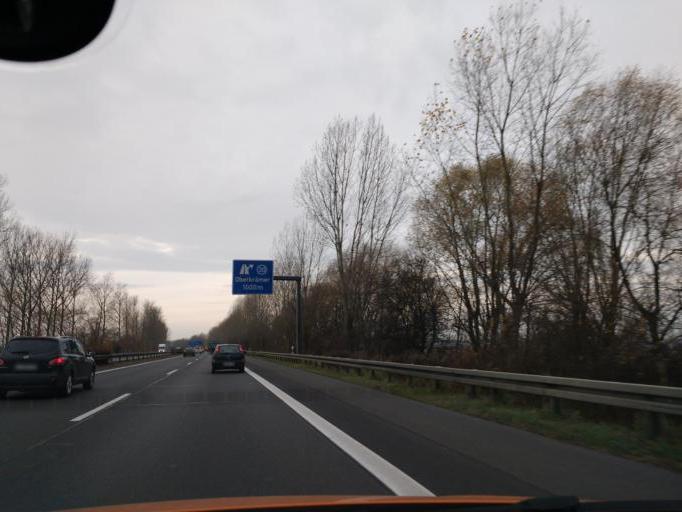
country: DE
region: Brandenburg
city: Velten
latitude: 52.7072
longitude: 13.1229
